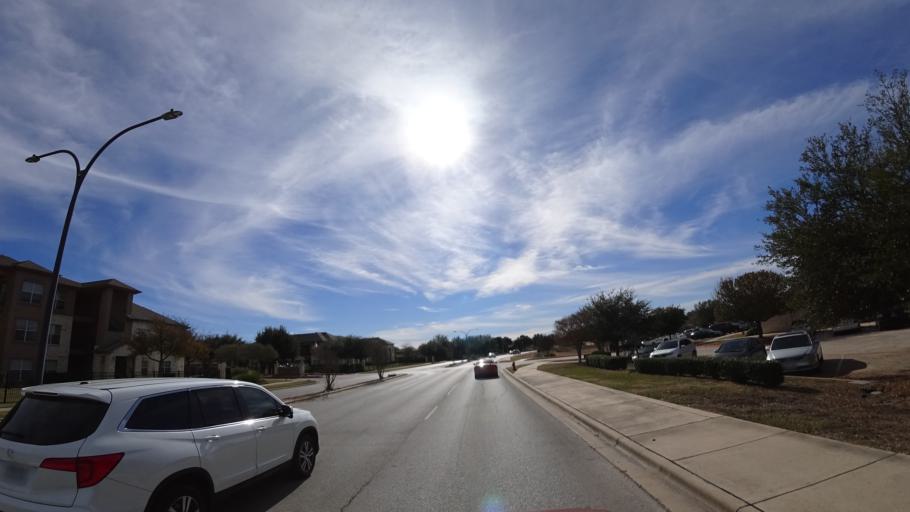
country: US
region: Texas
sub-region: Williamson County
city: Cedar Park
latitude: 30.5226
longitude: -97.8202
